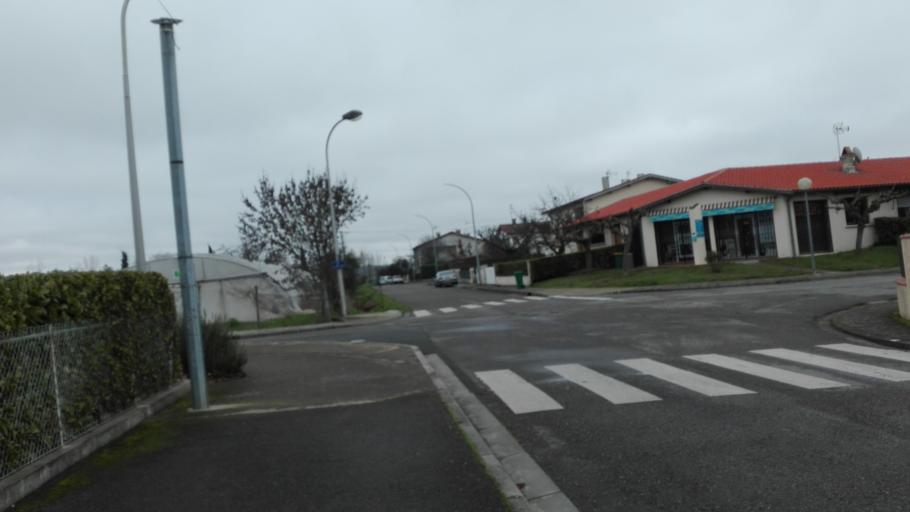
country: FR
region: Midi-Pyrenees
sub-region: Departement de la Haute-Garonne
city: Grenade
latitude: 43.7661
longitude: 1.2988
